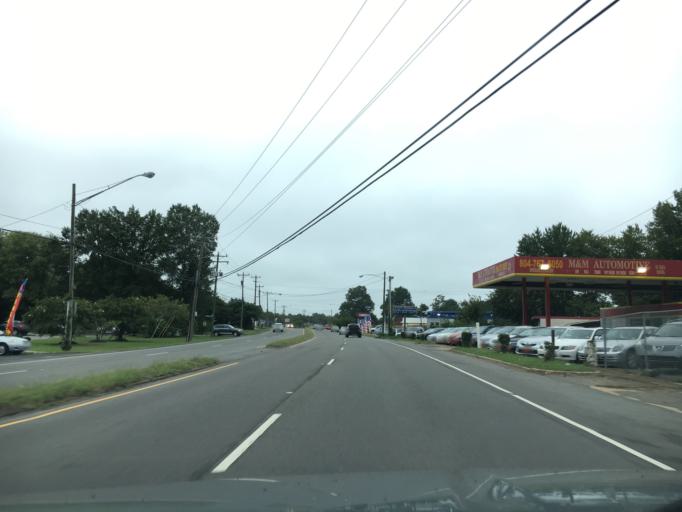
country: US
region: Virginia
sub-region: Chesterfield County
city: Bensley
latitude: 37.4897
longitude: -77.4930
